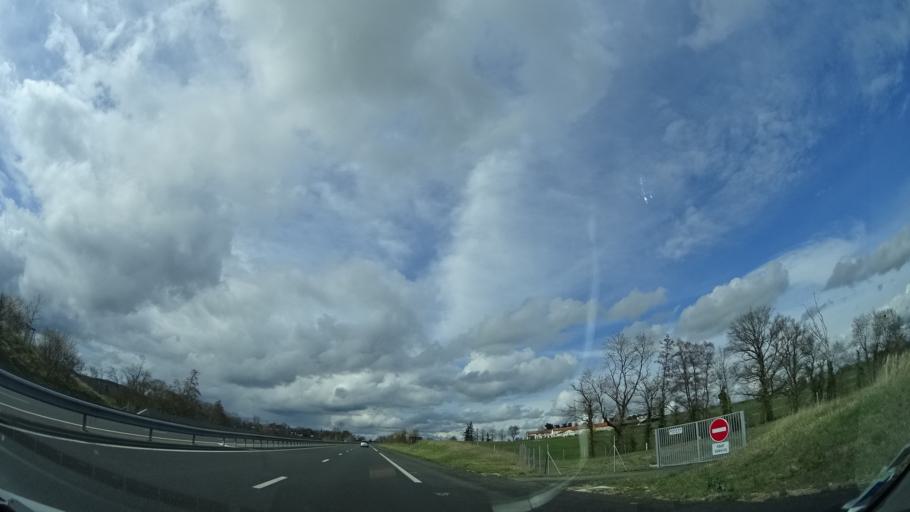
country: FR
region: Rhone-Alpes
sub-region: Departement de la Loire
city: La Pacaudiere
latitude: 46.1686
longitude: 3.8849
